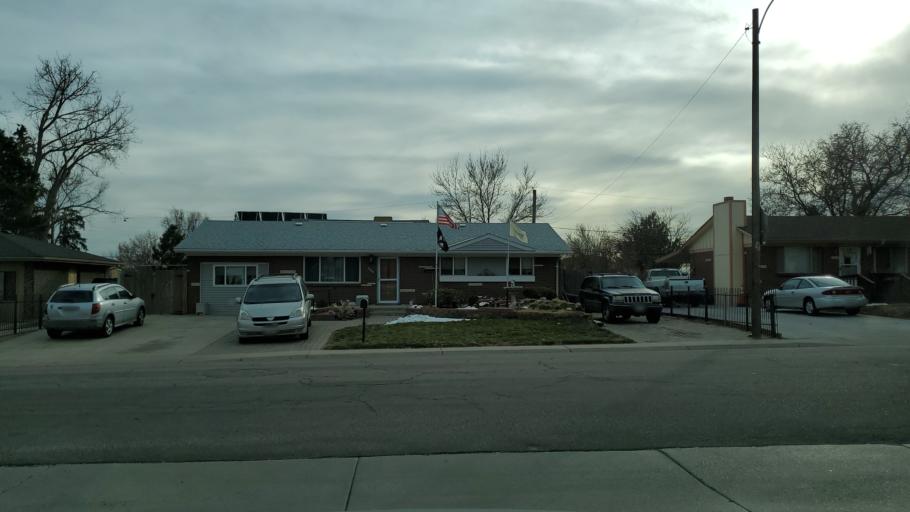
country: US
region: Colorado
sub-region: Adams County
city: Westminster
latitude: 39.8387
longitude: -105.0219
